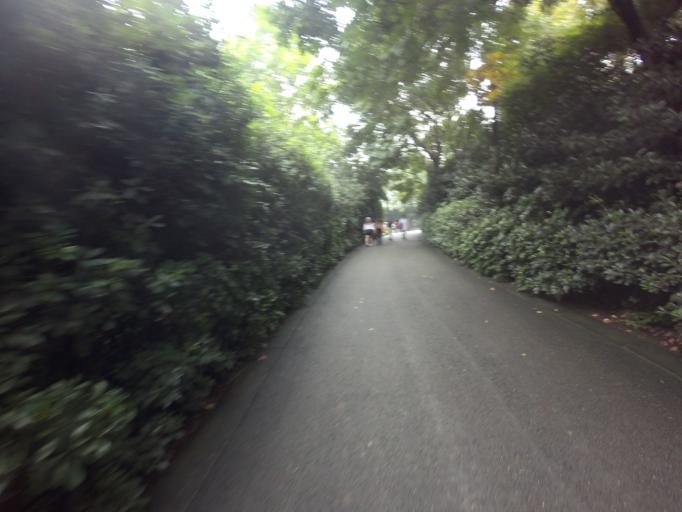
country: CN
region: Sichuan
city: Xindu
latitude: 30.7414
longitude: 104.1391
